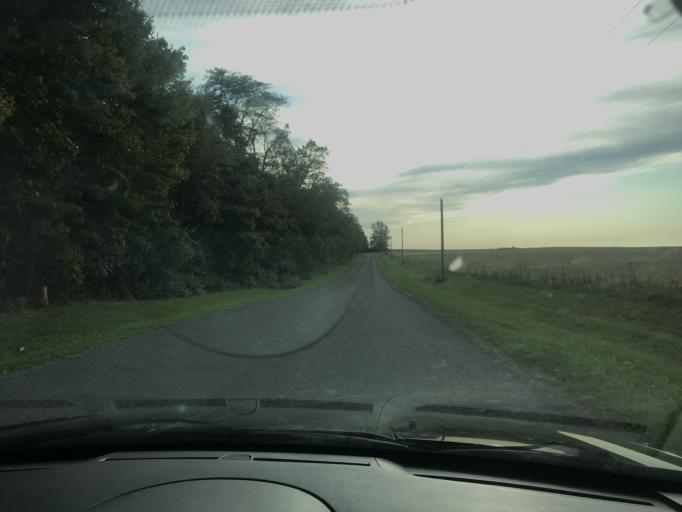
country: US
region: Ohio
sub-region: Champaign County
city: North Lewisburg
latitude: 40.2322
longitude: -83.6438
